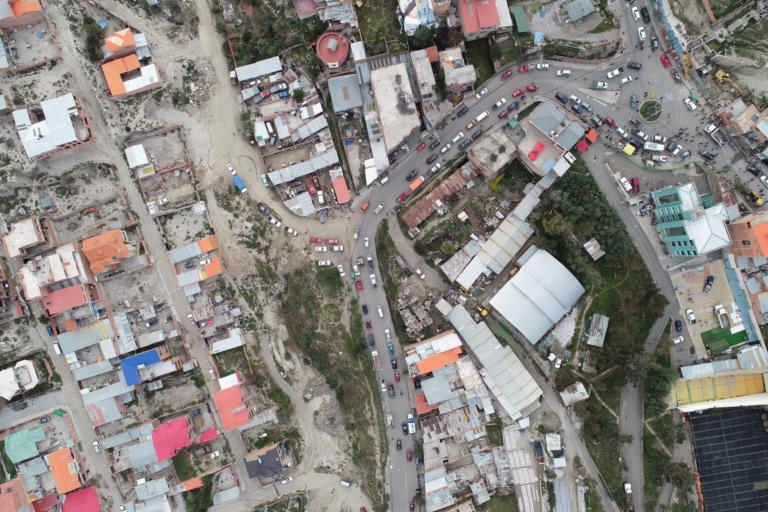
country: BO
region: La Paz
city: La Paz
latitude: -16.5210
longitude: -68.1253
